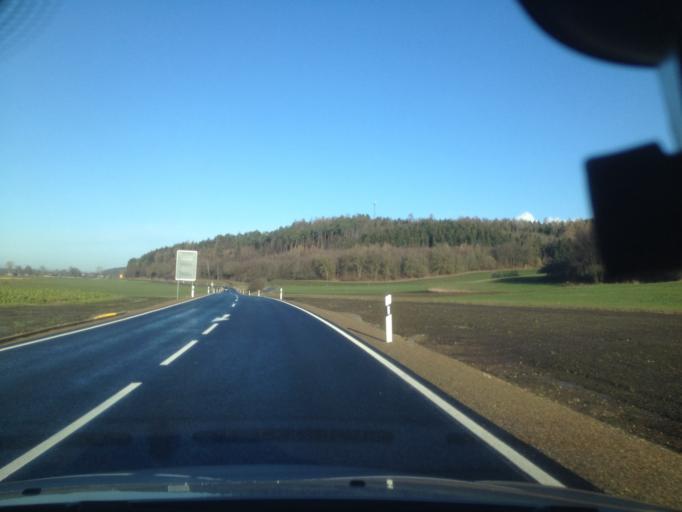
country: DE
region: Bavaria
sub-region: Swabia
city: Haldenwang
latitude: 48.4358
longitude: 10.4357
